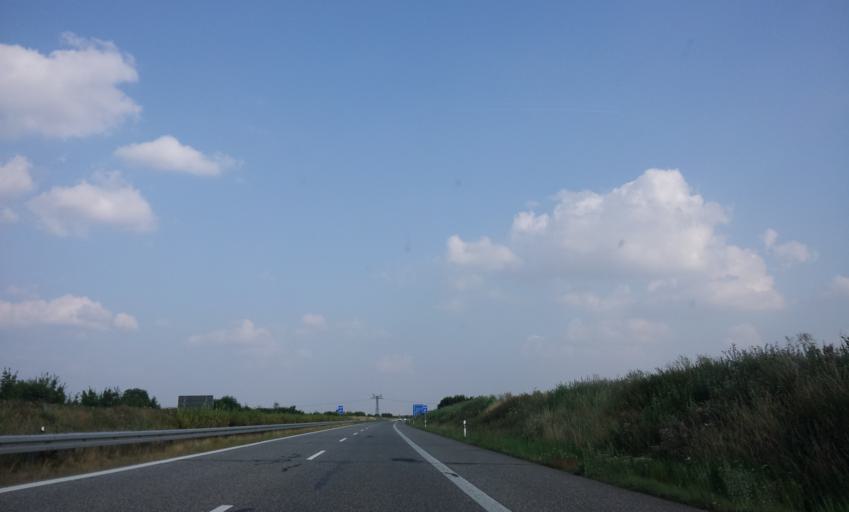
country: DE
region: Mecklenburg-Vorpommern
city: Jatznick
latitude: 53.5022
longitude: 13.9001
